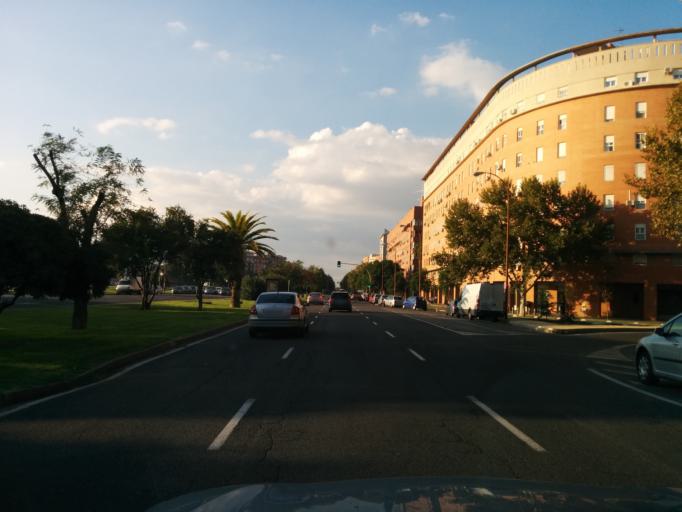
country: ES
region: Andalusia
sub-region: Provincia de Sevilla
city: Sevilla
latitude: 37.3939
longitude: -5.9210
